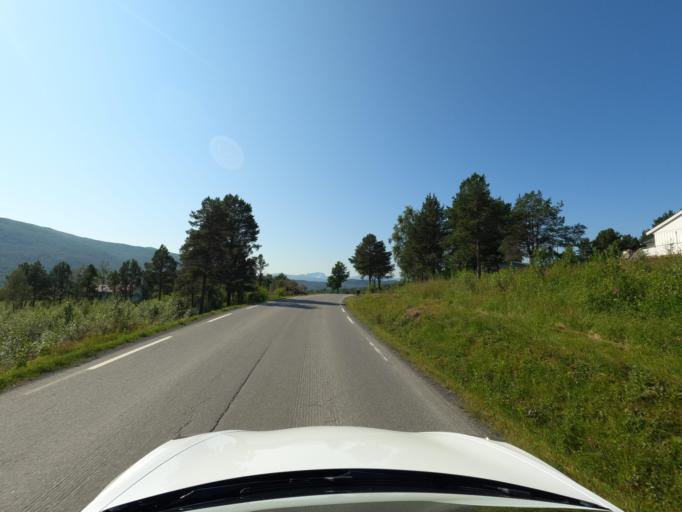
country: NO
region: Nordland
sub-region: Ballangen
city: Ballangen
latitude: 68.3508
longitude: 16.8595
